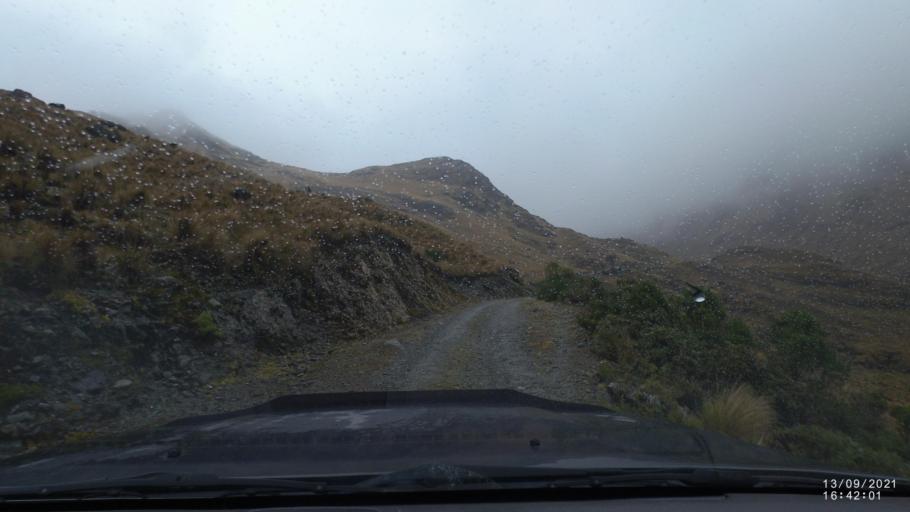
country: BO
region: Cochabamba
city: Colomi
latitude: -17.2858
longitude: -65.7116
